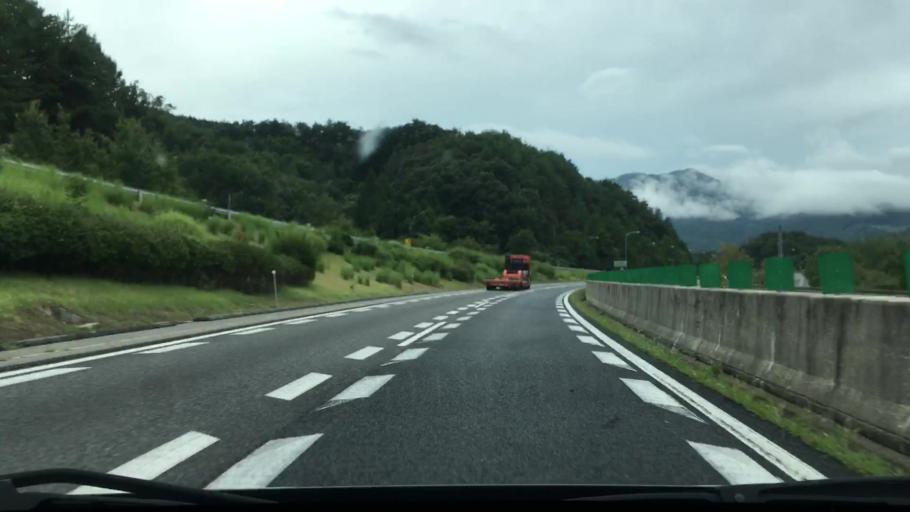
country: JP
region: Hiroshima
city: Hiroshima-shi
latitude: 34.5876
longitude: 132.4824
